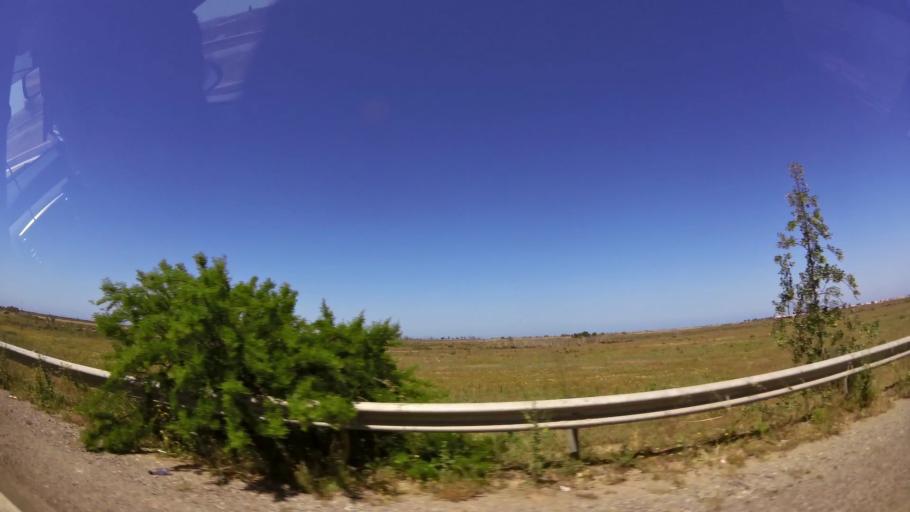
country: MA
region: Oriental
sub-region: Berkane-Taourirt
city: Madagh
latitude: 35.1047
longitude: -2.3438
